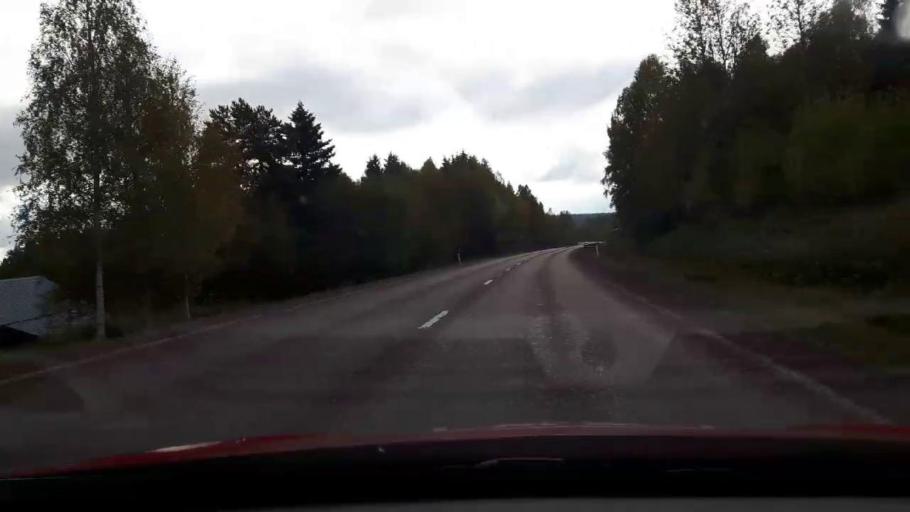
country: SE
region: Gaevleborg
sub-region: Ljusdals Kommun
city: Jaervsoe
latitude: 61.6139
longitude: 16.2953
